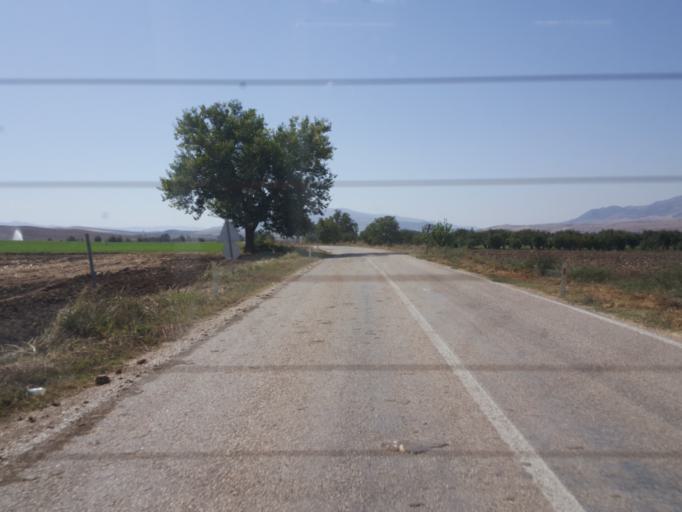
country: TR
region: Amasya
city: Dogantepe
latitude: 40.5308
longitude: 35.6670
